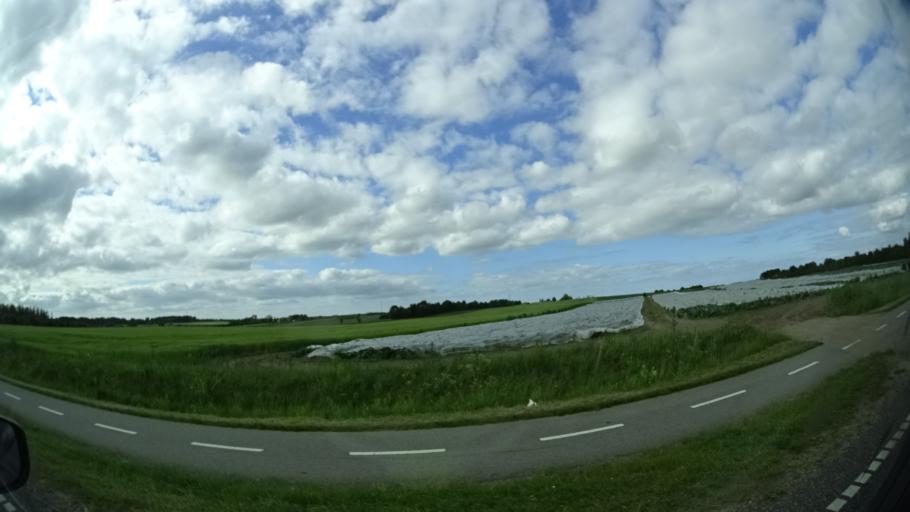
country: DK
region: Central Jutland
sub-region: Syddjurs Kommune
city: Ryomgard
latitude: 56.4378
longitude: 10.6603
